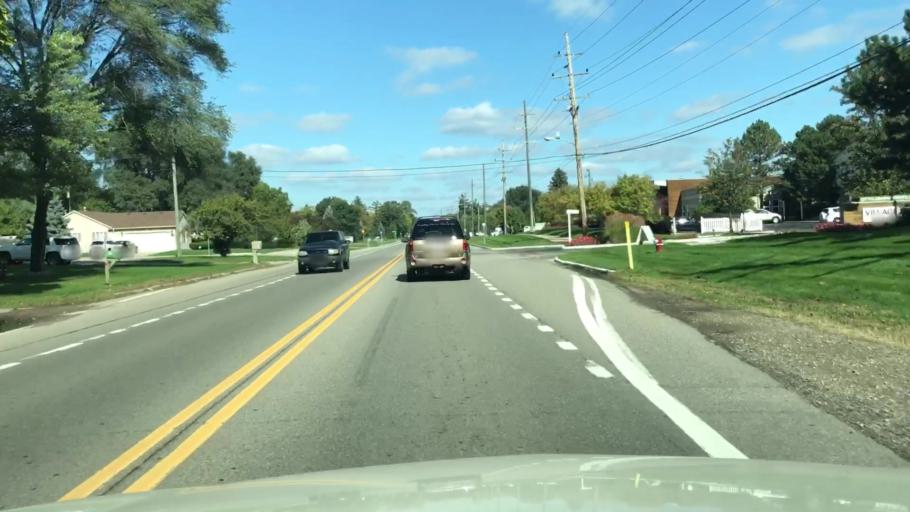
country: US
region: Michigan
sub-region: Macomb County
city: Utica
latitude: 42.6327
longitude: -83.0918
